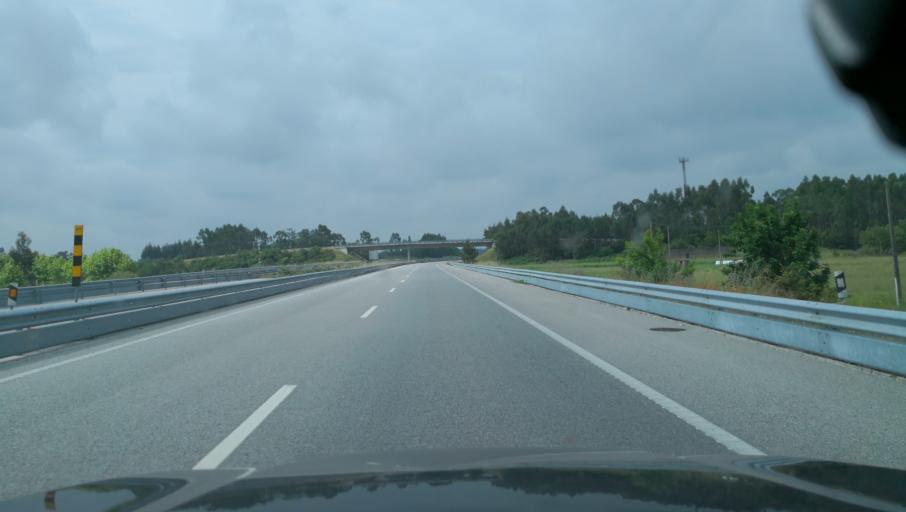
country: PT
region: Coimbra
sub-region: Figueira da Foz
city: Alhadas
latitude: 40.2604
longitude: -8.7616
